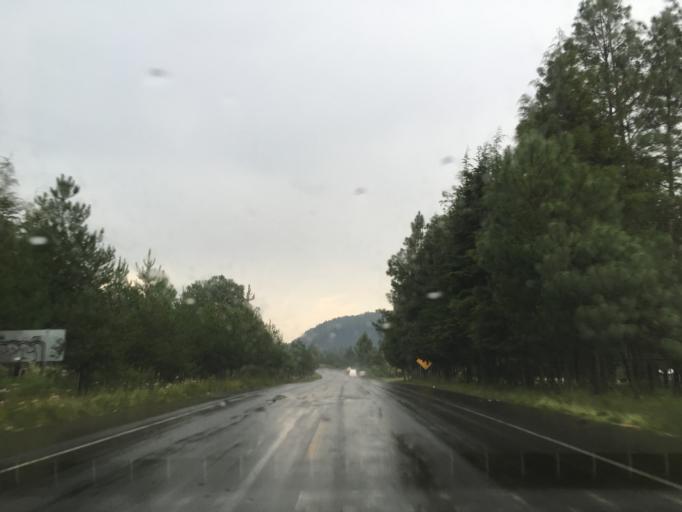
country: MX
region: Michoacan
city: Angahuan
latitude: 19.5427
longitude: -102.2061
